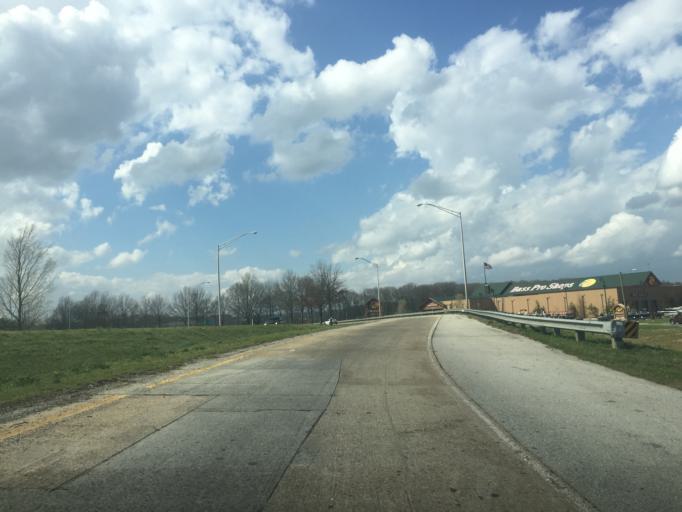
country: US
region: Georgia
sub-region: Catoosa County
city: Indian Springs
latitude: 34.9906
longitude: -85.2018
